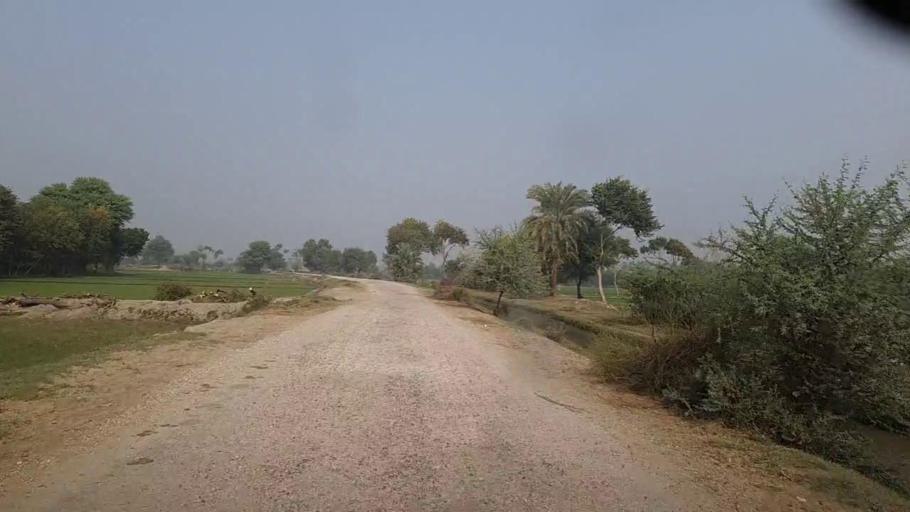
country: PK
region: Sindh
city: Bozdar
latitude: 27.0645
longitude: 68.6367
